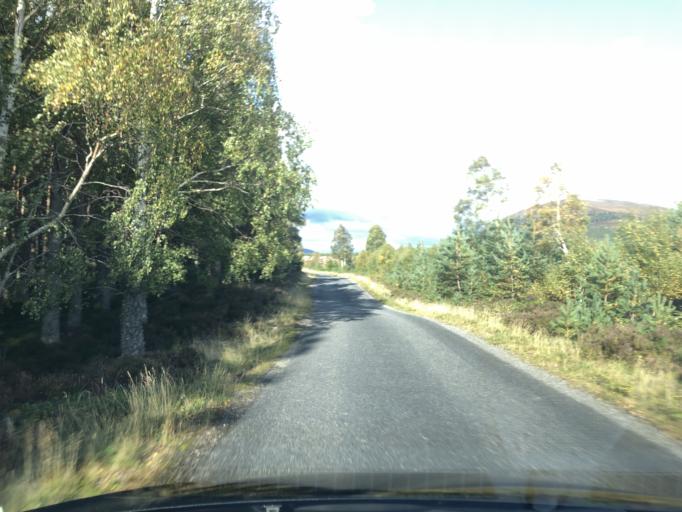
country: GB
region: Scotland
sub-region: Highland
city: Aviemore
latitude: 57.0747
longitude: -3.9013
